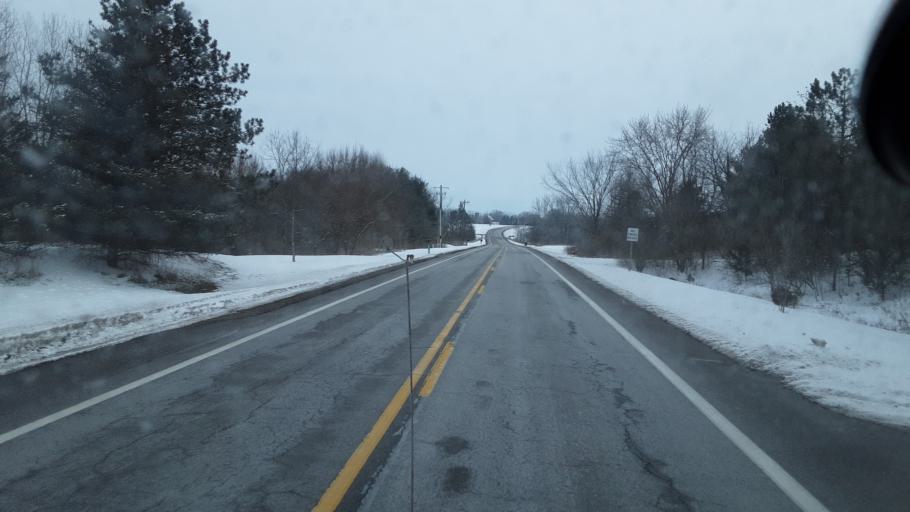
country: US
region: Ohio
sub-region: Madison County
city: Plain City
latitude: 40.1372
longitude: -83.2897
